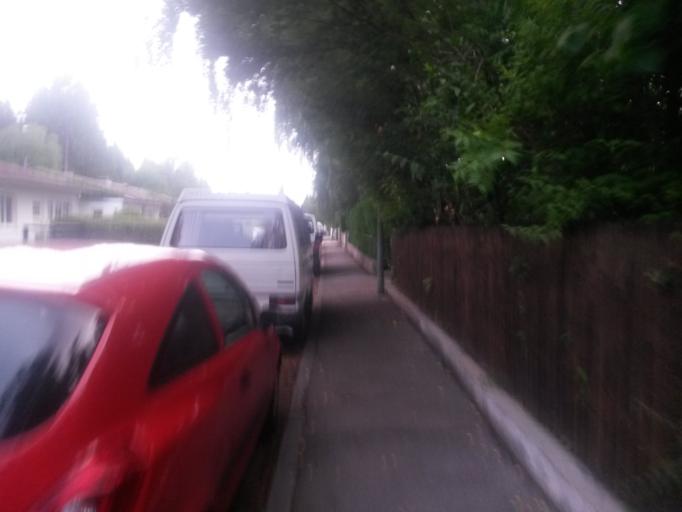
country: DE
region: Bavaria
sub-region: Upper Bavaria
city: Neubiberg
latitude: 48.1001
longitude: 11.6714
